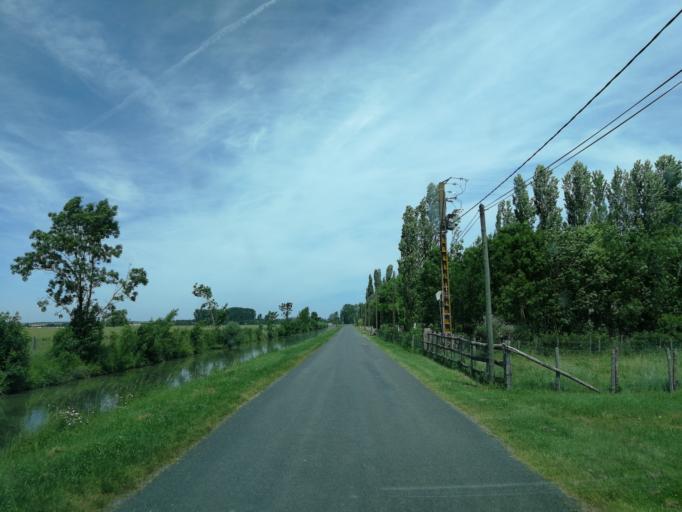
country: FR
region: Pays de la Loire
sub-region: Departement de la Vendee
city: Le Langon
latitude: 46.4123
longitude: -0.9208
